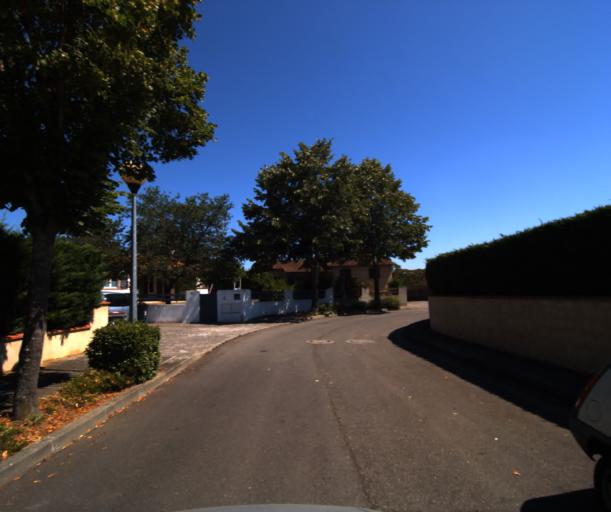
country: FR
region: Midi-Pyrenees
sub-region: Departement de la Haute-Garonne
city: Seysses
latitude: 43.4682
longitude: 1.3089
